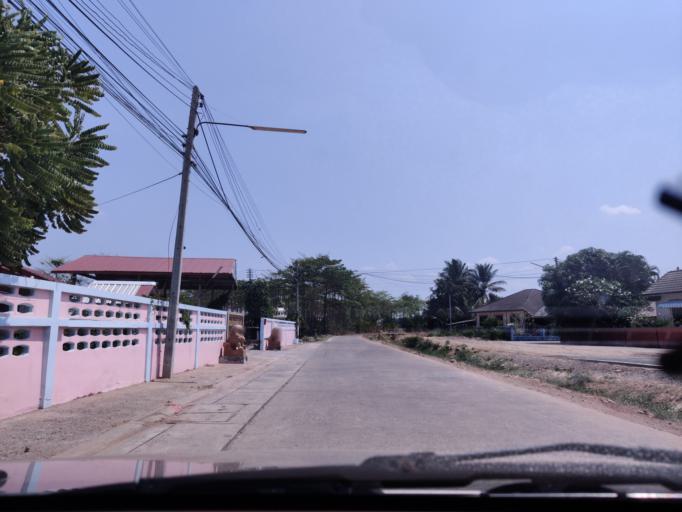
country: TH
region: Sisaket
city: Si Sa Ket
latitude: 15.1079
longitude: 104.3542
